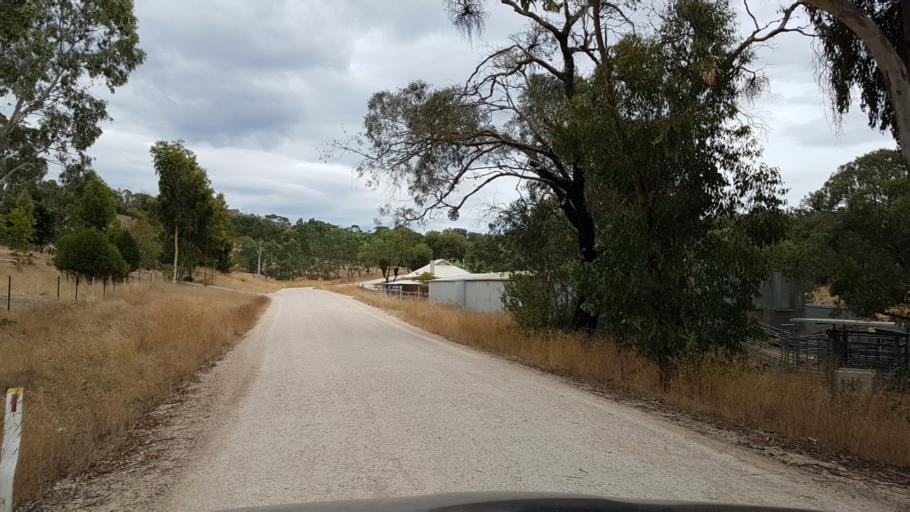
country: AU
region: South Australia
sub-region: Adelaide Hills
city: Gumeracha
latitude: -34.8018
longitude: 138.8331
